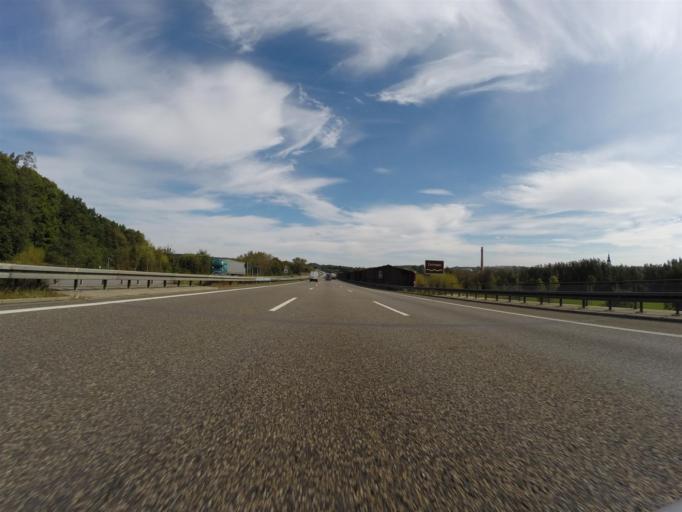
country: DE
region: Saxony
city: Frankenberg
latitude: 50.9157
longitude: 13.0223
